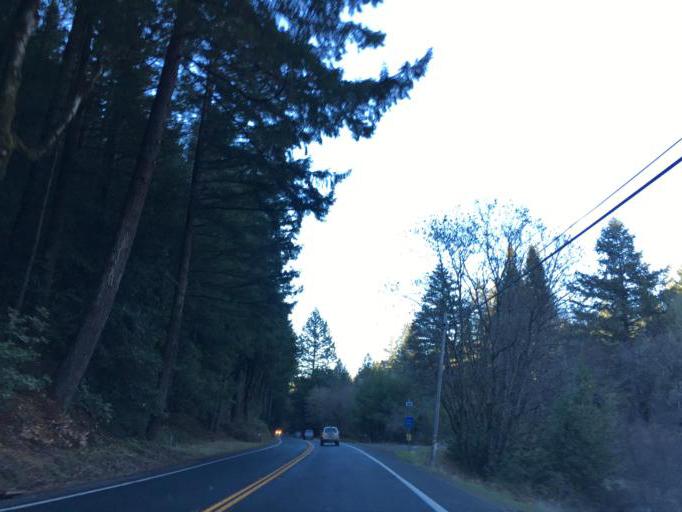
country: US
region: California
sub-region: Mendocino County
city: Brooktrails
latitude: 39.5070
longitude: -123.3815
